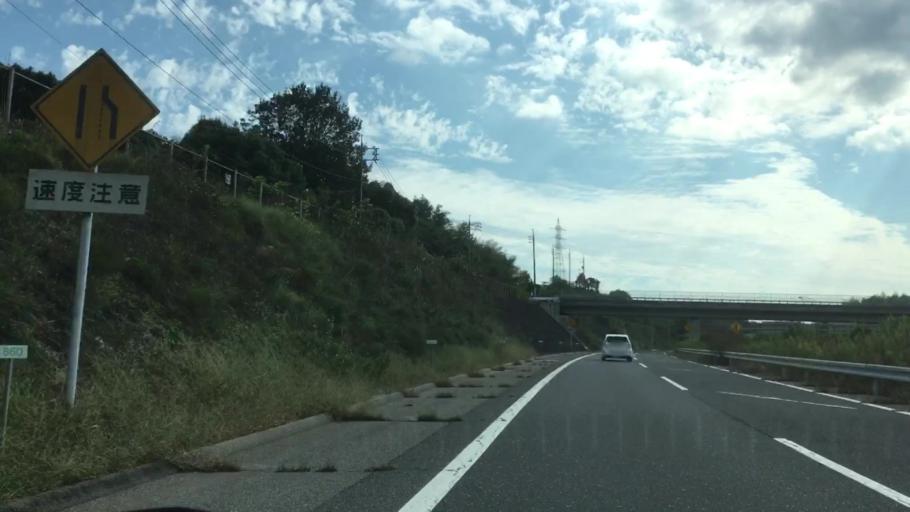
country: JP
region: Hiroshima
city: Hatsukaichi
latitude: 34.3323
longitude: 132.2946
